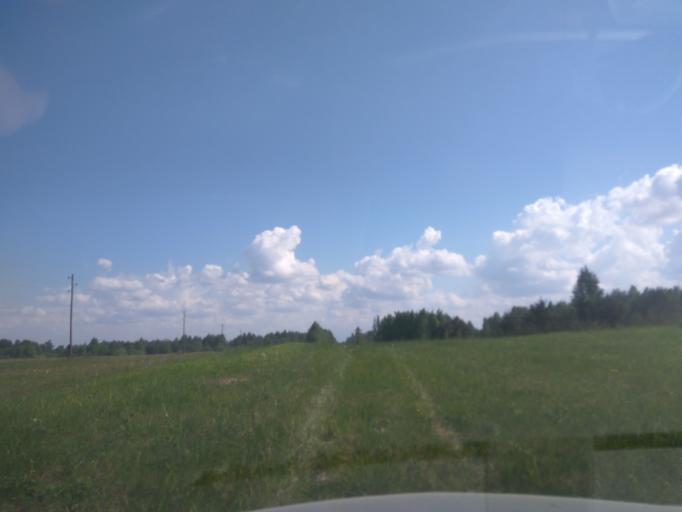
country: LV
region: Kuldigas Rajons
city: Kuldiga
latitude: 57.1778
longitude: 22.0086
